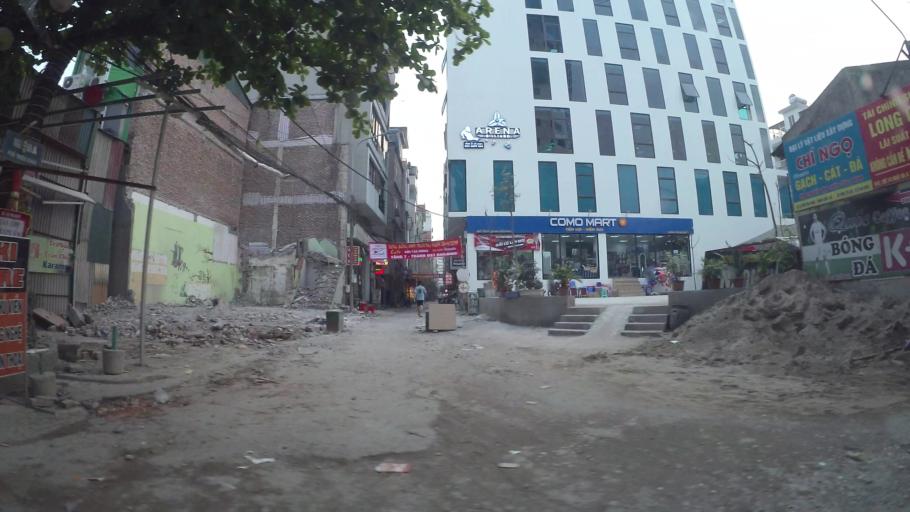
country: VN
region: Ha Noi
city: Thanh Xuan
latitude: 20.9840
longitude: 105.8000
